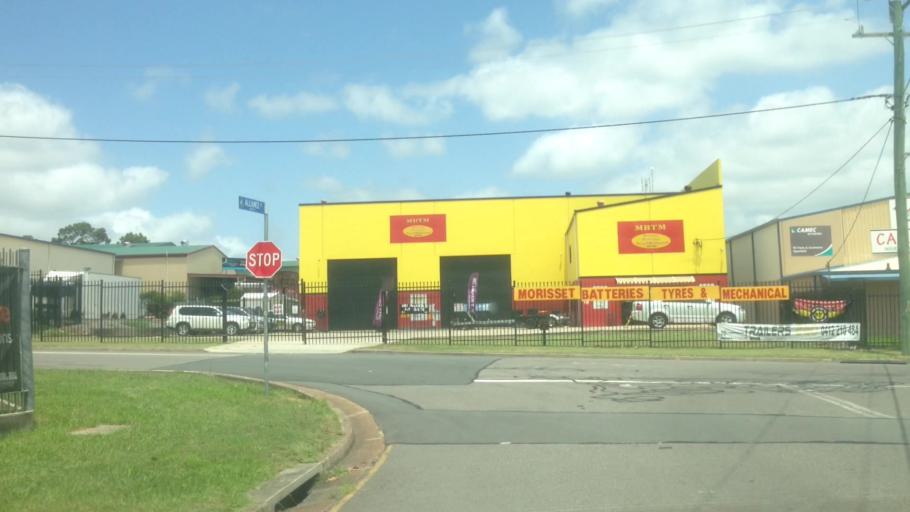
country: AU
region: New South Wales
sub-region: Lake Macquarie Shire
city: Dora Creek
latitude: -33.1173
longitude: 151.4724
